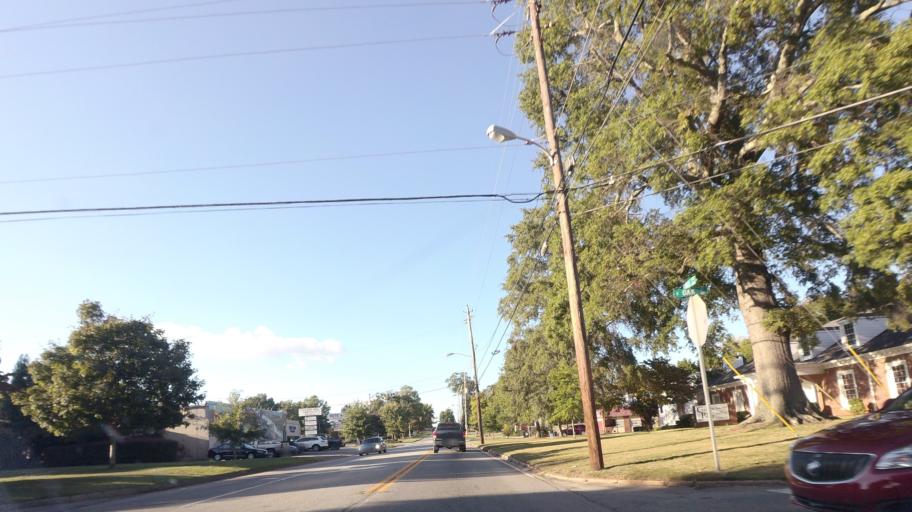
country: US
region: Georgia
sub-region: Spalding County
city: Griffin
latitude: 33.2431
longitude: -84.2640
